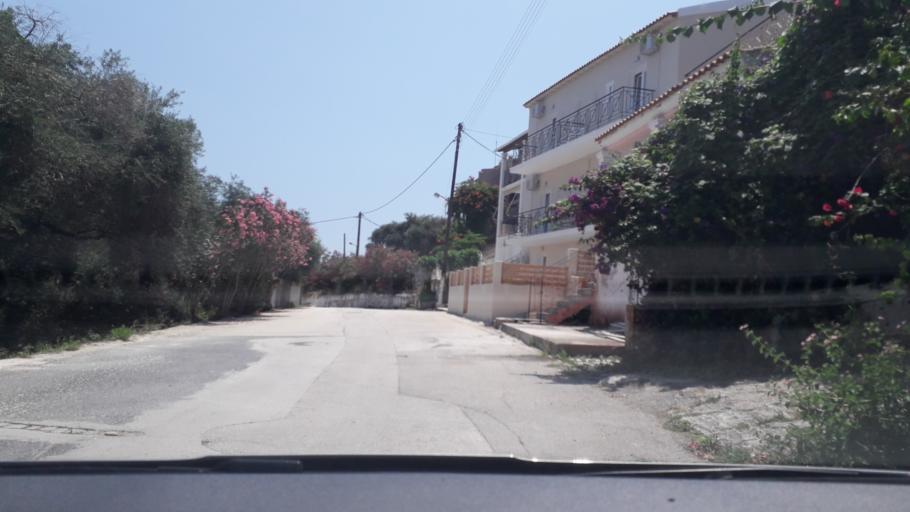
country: GR
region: Ionian Islands
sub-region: Nomos Kerkyras
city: Lefkimmi
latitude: 39.3809
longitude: 20.1146
